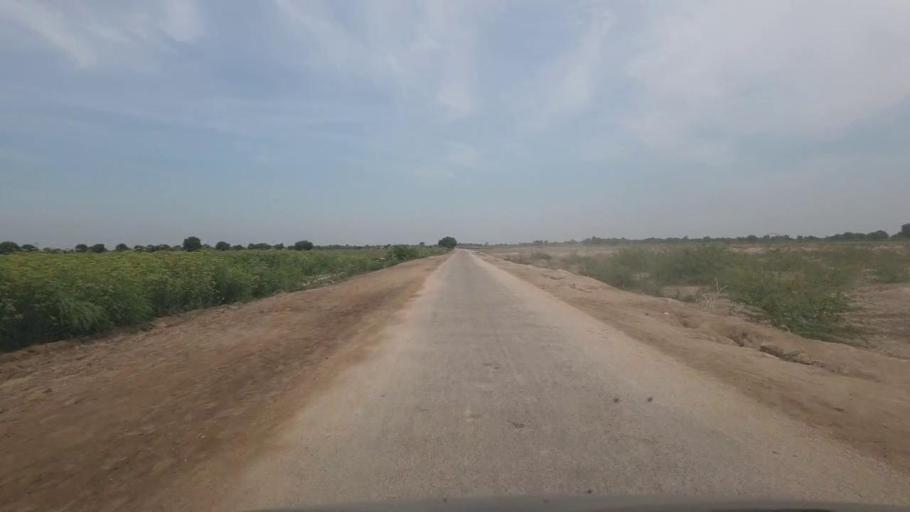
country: PK
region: Sindh
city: Kunri
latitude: 25.2446
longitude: 69.6179
